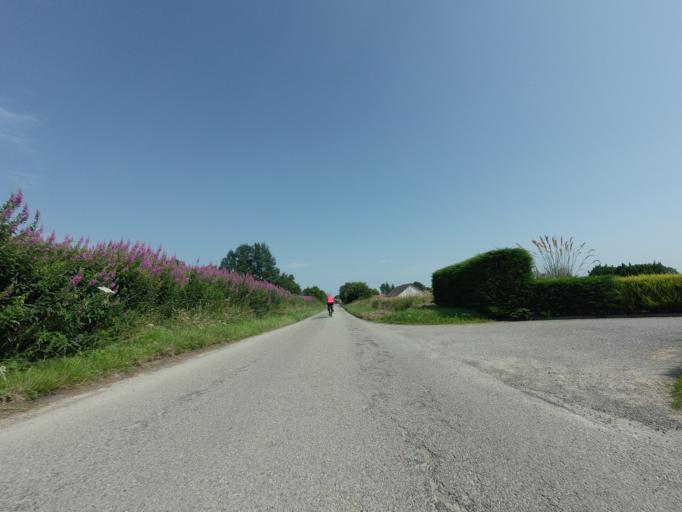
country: GB
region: Scotland
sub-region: Highland
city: Tain
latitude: 57.8003
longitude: -4.0678
